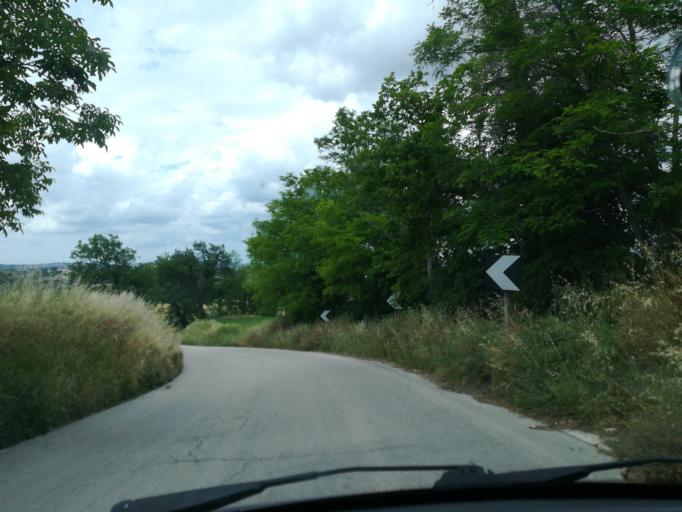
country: IT
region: The Marches
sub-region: Provincia di Macerata
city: Petriolo
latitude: 43.2287
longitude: 13.4620
